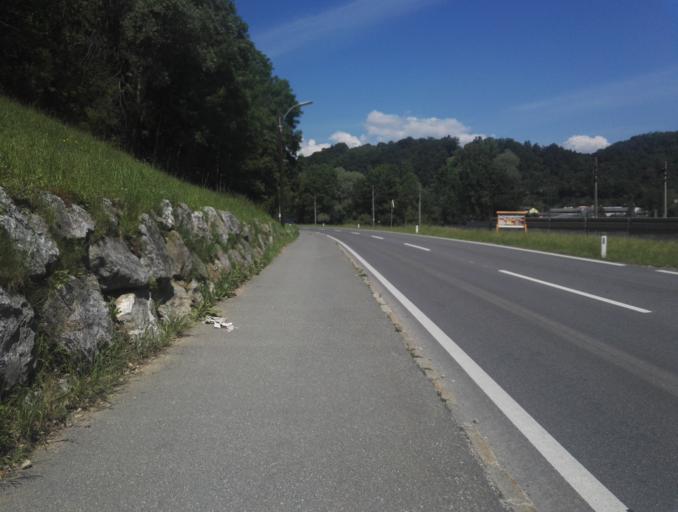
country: AT
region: Styria
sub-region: Politischer Bezirk Graz-Umgebung
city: Gratkorn
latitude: 47.1169
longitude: 15.3689
